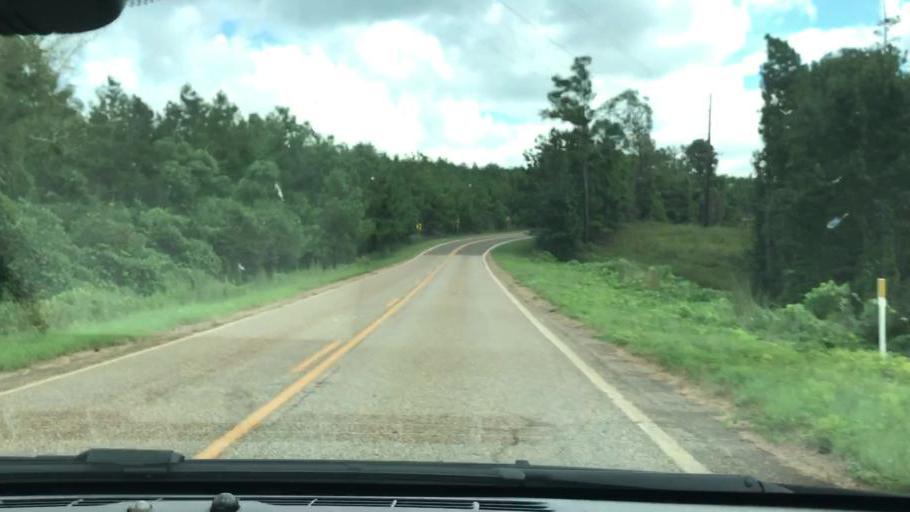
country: US
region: Georgia
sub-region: Stewart County
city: Lumpkin
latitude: 32.0727
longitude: -84.8780
